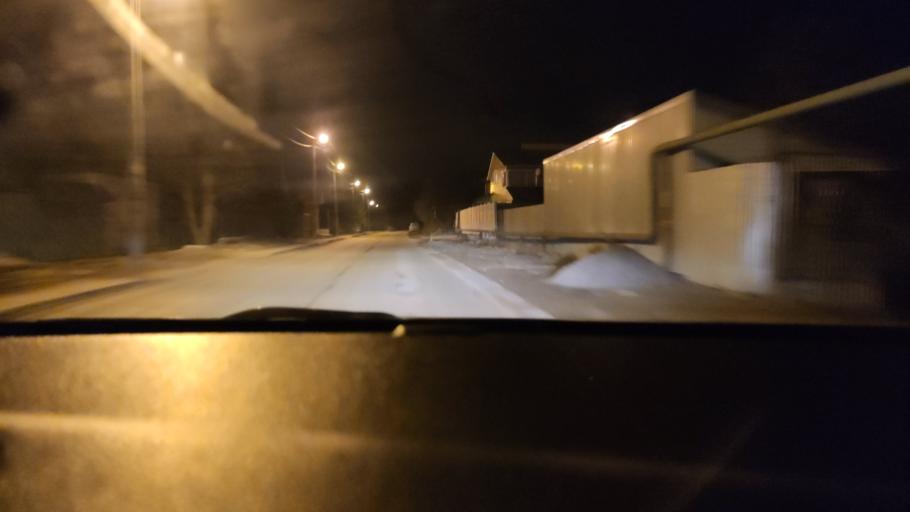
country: RU
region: Tatarstan
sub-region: Gorod Kazan'
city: Kazan
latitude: 55.8454
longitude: 49.1986
